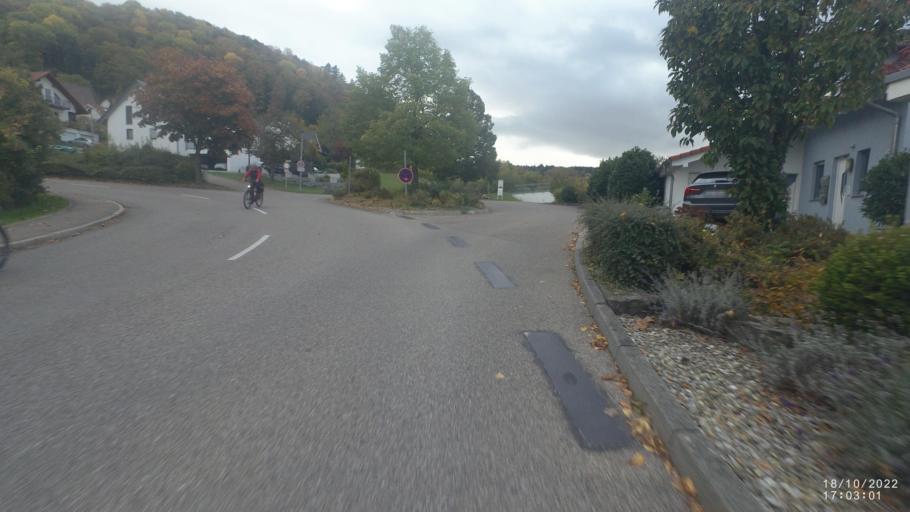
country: DE
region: Baden-Wuerttemberg
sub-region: Regierungsbezirk Stuttgart
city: Aichelberg
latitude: 48.6345
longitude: 9.5661
